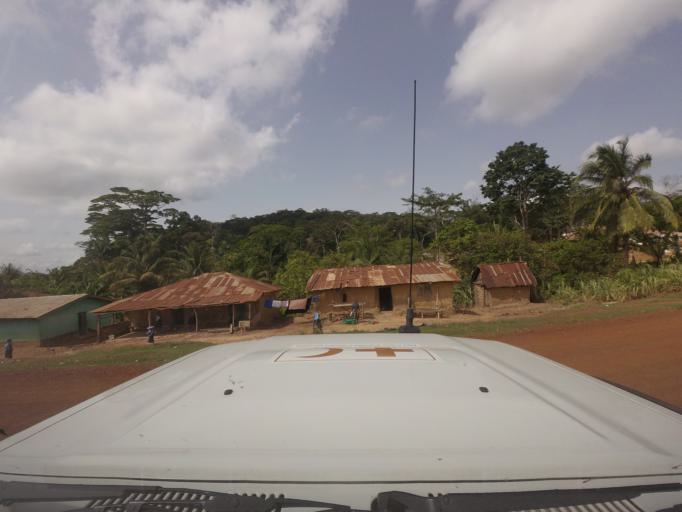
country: LR
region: Bong
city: Gbarnga
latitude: 7.2614
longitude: -9.4359
